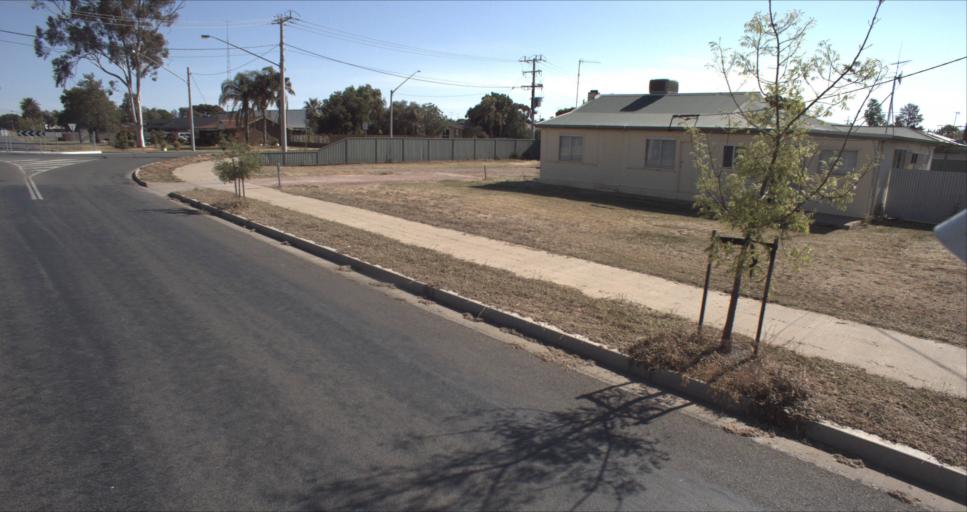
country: AU
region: New South Wales
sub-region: Leeton
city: Leeton
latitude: -34.5564
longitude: 146.4162
